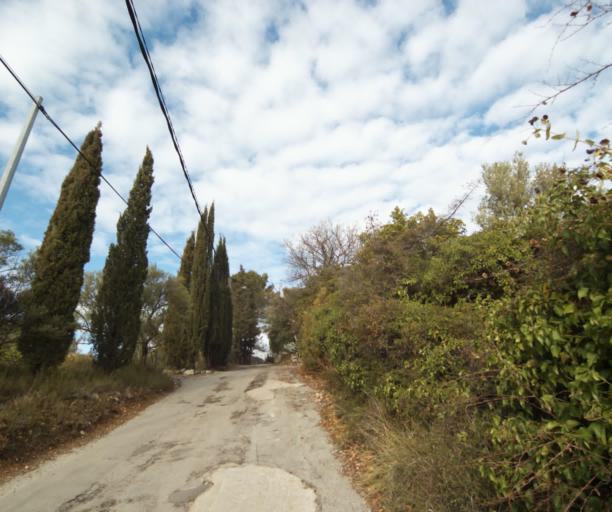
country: FR
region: Provence-Alpes-Cote d'Azur
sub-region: Departement du Var
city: Trans-en-Provence
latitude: 43.5023
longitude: 6.4814
